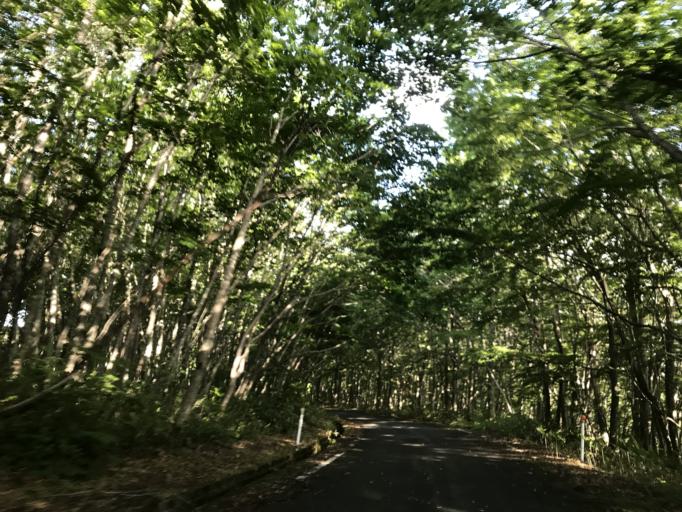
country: JP
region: Iwate
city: Ichinoseki
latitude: 38.9187
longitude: 140.8463
